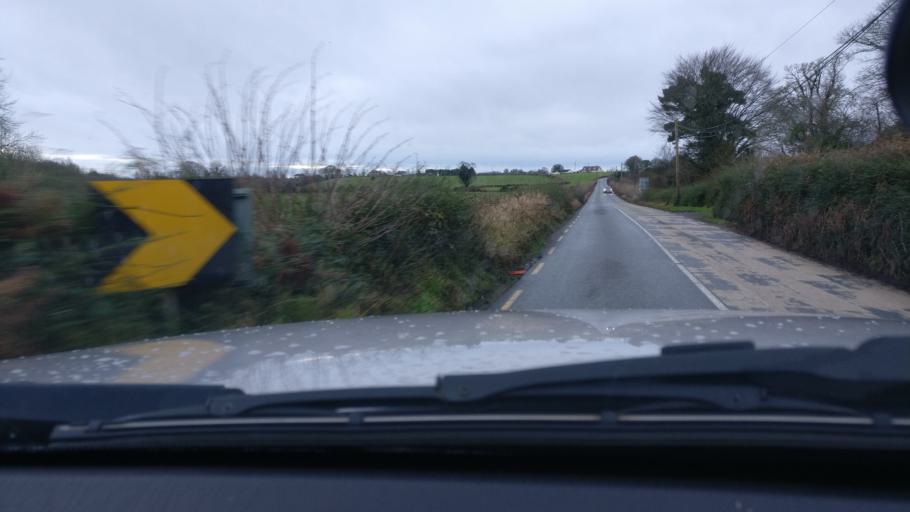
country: IE
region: Leinster
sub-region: An Longfort
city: Granard
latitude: 53.7966
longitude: -7.3901
